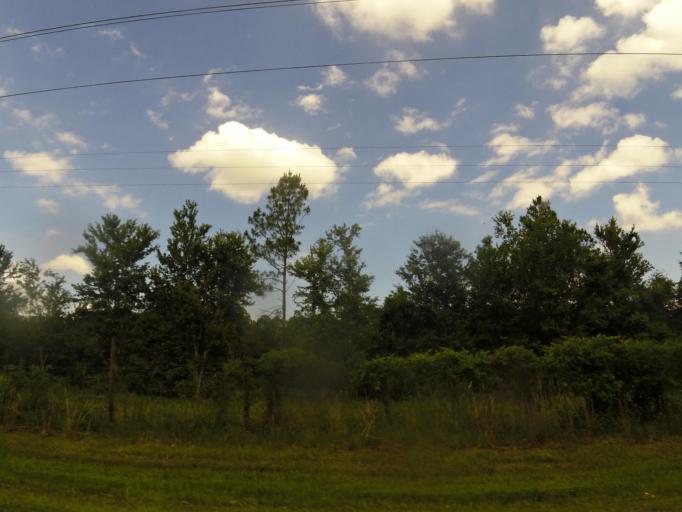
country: US
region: Florida
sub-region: Clay County
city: Green Cove Springs
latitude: 29.9670
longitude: -81.7393
